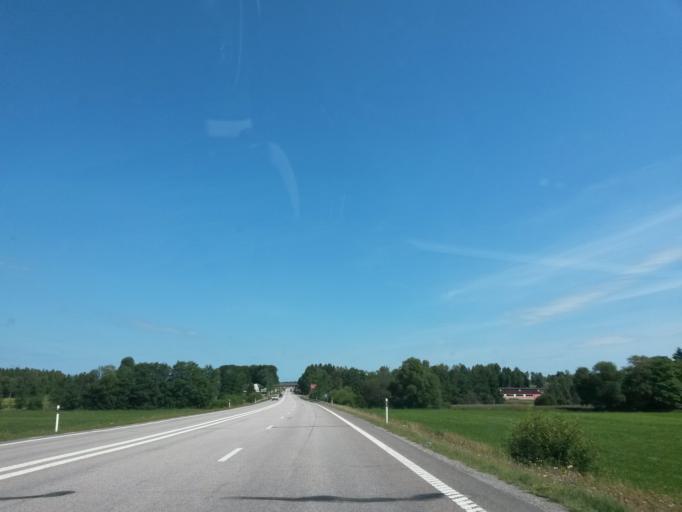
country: SE
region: Vaestra Goetaland
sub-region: Vargarda Kommun
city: Vargarda
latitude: 58.0258
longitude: 12.7842
